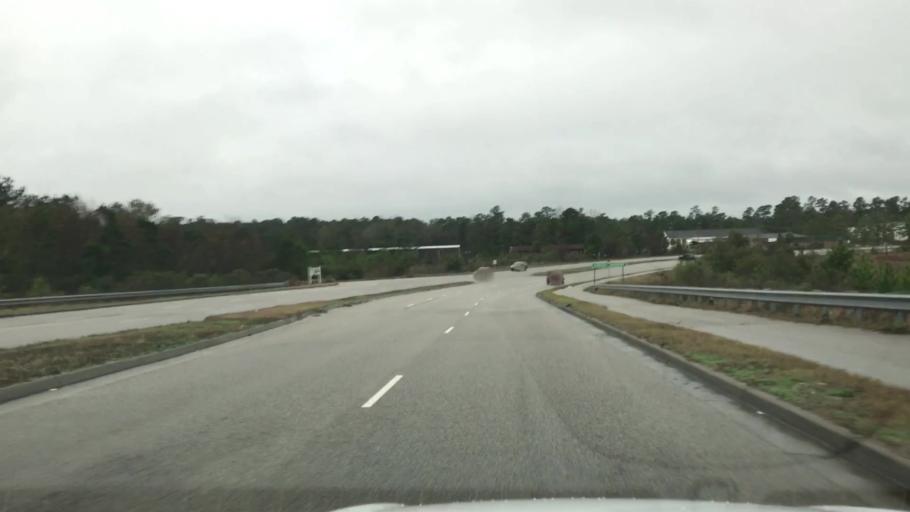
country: US
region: South Carolina
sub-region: Horry County
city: Forestbrook
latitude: 33.7078
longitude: -78.9386
